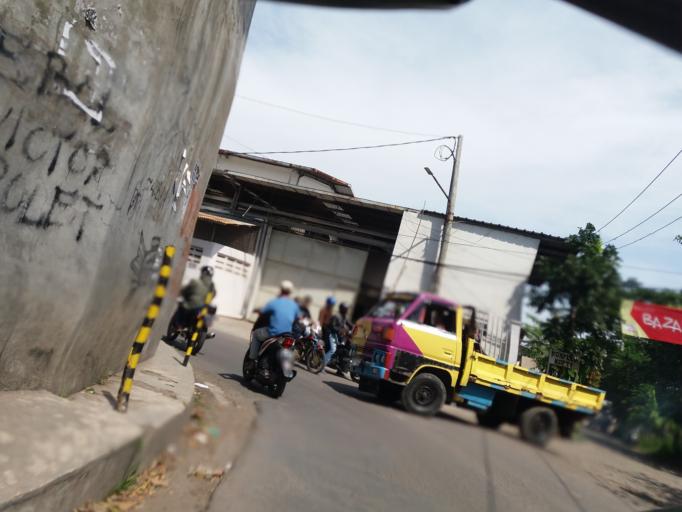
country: ID
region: West Java
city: Margahayukencana
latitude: -6.9458
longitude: 107.5678
